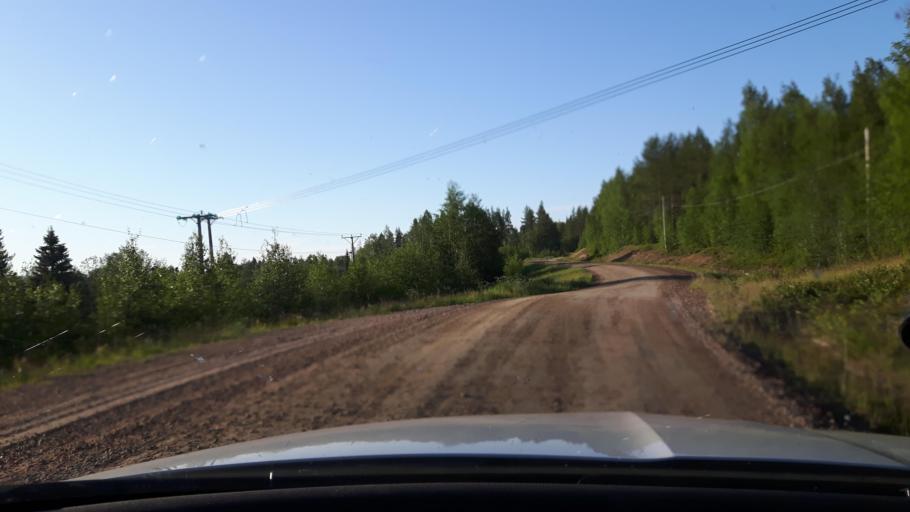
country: SE
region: Vaesternorrland
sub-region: Ange Kommun
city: Ange
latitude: 62.1775
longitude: 15.6331
